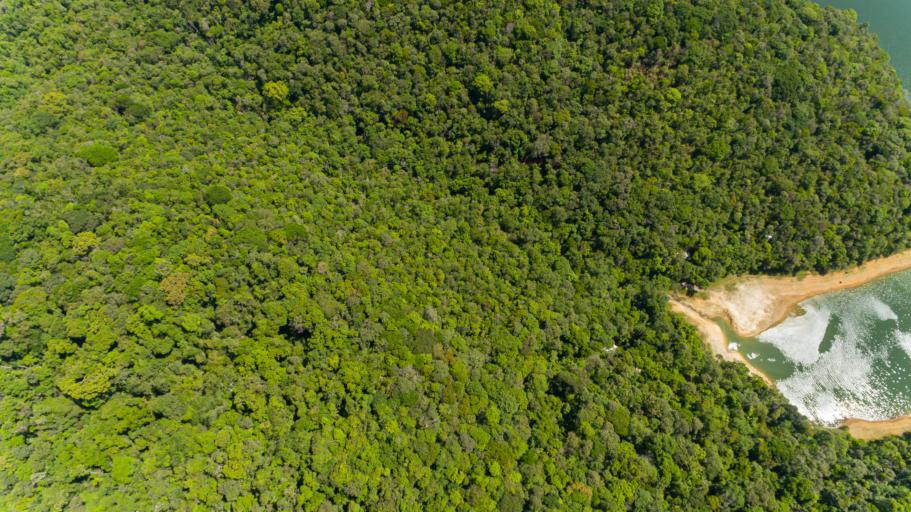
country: BR
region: Sao Paulo
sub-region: Juquitiba
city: Juquitiba
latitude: -24.0247
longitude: -47.2481
